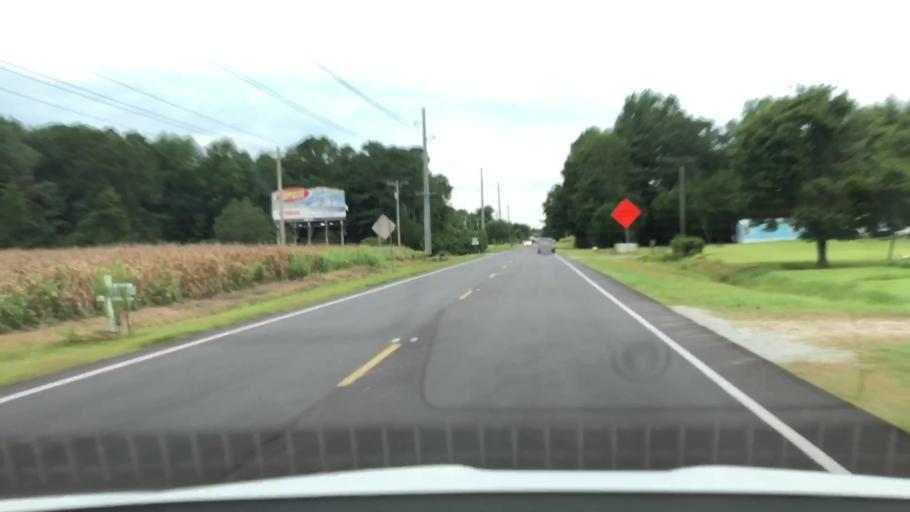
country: US
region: North Carolina
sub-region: Jones County
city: Maysville
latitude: 34.8331
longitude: -77.1642
